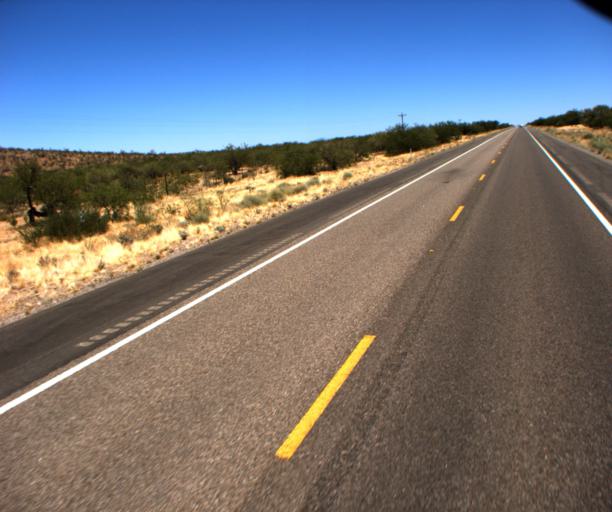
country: US
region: Arizona
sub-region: Pima County
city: Sells
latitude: 32.0168
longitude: -111.6287
